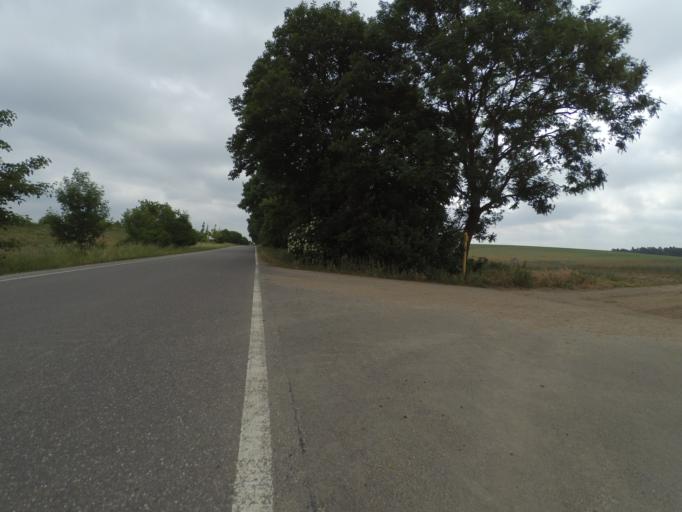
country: DE
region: Mecklenburg-Vorpommern
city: Krakow am See
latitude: 53.6347
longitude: 12.3647
